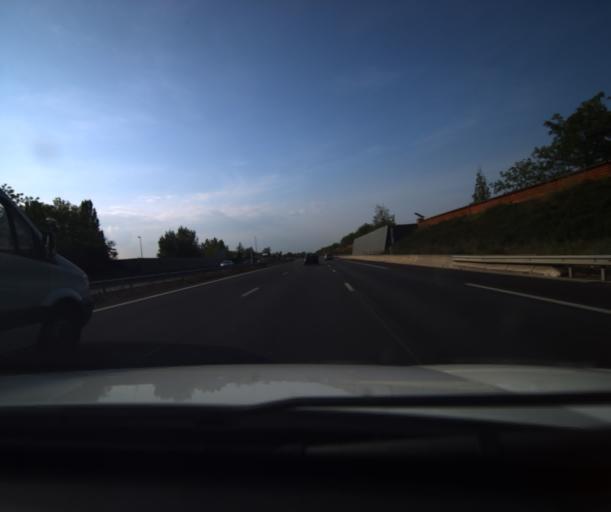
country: FR
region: Midi-Pyrenees
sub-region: Departement de la Haute-Garonne
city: Saint-Alban
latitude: 43.6908
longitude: 1.4111
